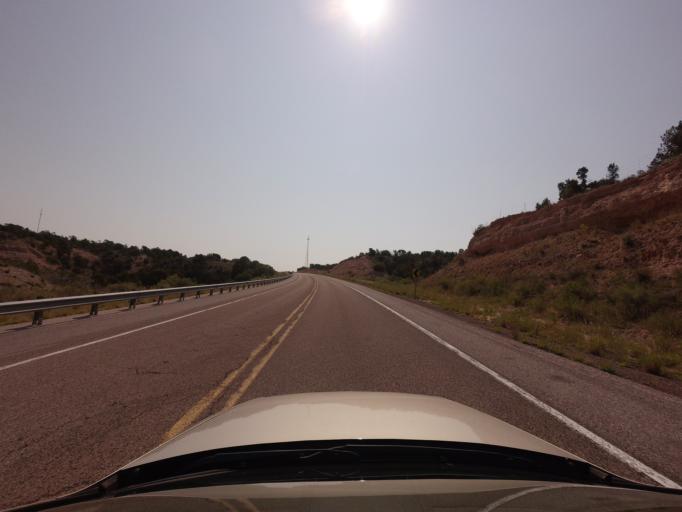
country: US
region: New Mexico
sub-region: Quay County
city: Tucumcari
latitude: 34.8233
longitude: -103.7481
